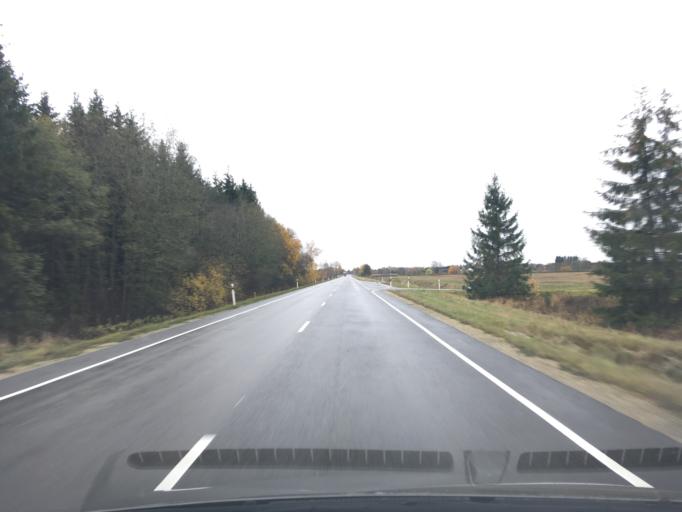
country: EE
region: Jogevamaa
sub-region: Tabivere vald
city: Tabivere
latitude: 58.4414
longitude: 26.5044
